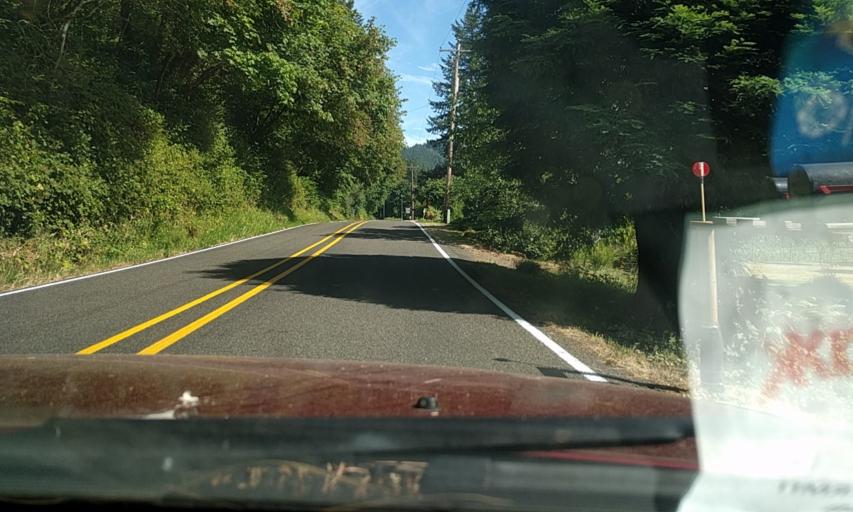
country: US
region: Oregon
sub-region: Lane County
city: Florence
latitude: 44.0408
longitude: -123.8645
